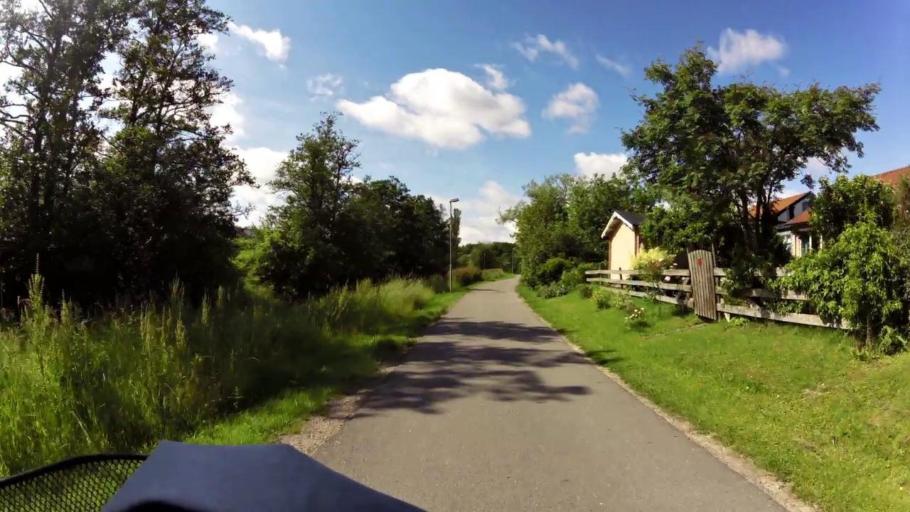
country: SE
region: OEstergoetland
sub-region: Linkopings Kommun
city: Linkoping
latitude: 58.3872
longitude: 15.6404
